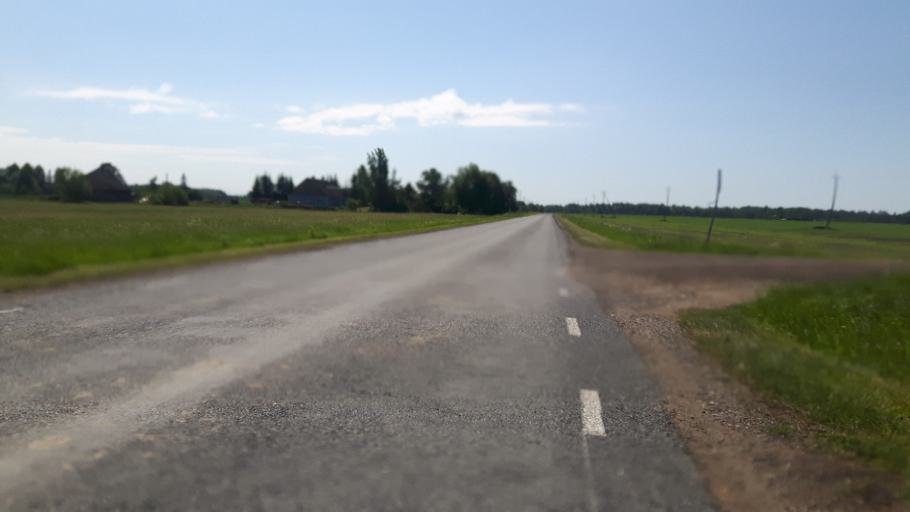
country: EE
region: Paernumaa
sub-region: Vaendra vald (alev)
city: Vandra
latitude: 58.6150
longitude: 25.0213
